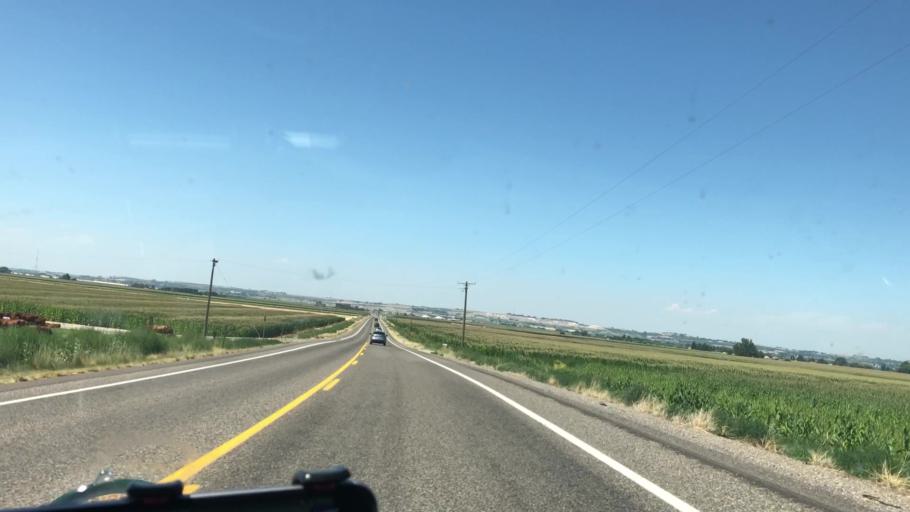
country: US
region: Idaho
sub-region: Owyhee County
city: Marsing
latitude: 43.5227
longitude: -116.8515
